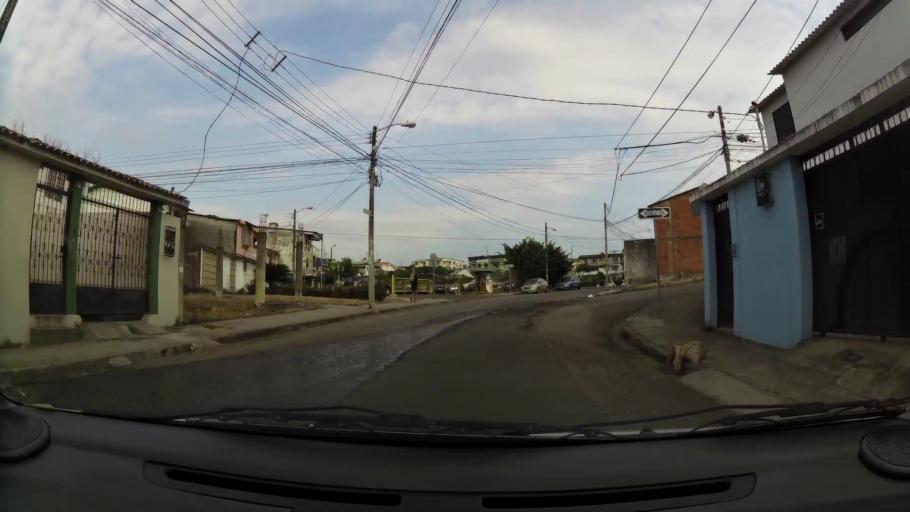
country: EC
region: Guayas
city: Eloy Alfaro
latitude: -2.1310
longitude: -79.8942
